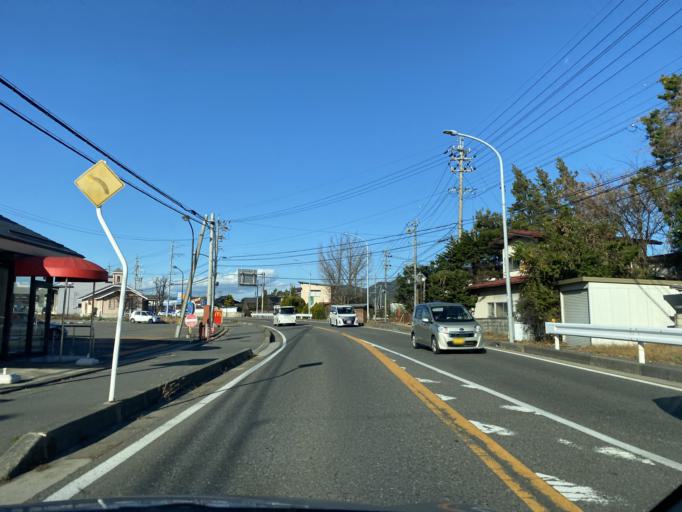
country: JP
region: Nagano
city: Omachi
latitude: 36.4825
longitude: 137.8518
